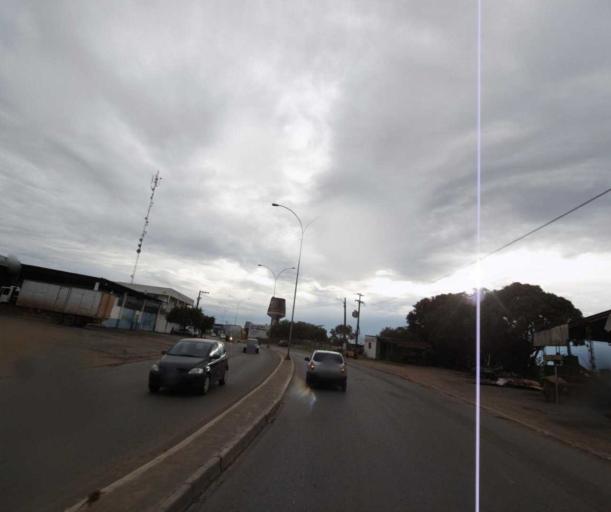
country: BR
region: Mato Grosso
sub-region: Varzea Grande
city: Varzea Grande
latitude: -15.6468
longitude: -56.1424
